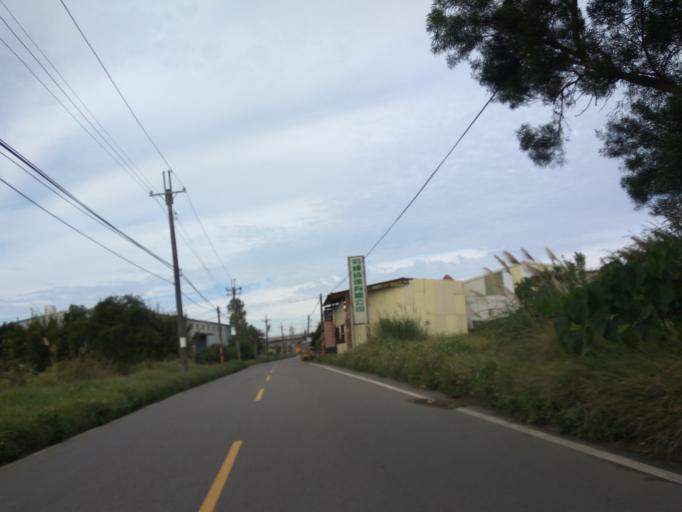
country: TW
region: Taiwan
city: Taoyuan City
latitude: 24.9491
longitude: 121.1418
